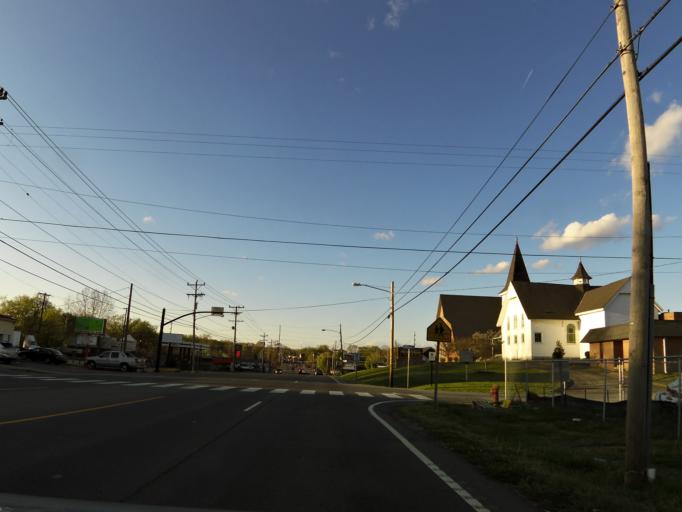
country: US
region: Tennessee
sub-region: Davidson County
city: Goodlettsville
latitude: 36.3186
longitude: -86.7131
